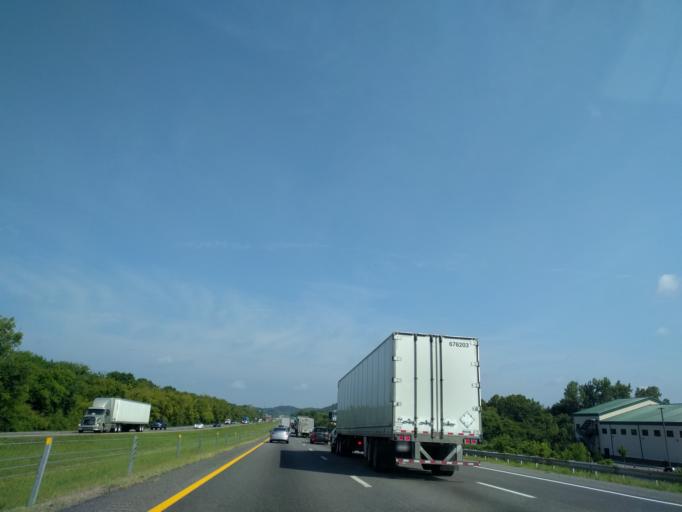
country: US
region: Tennessee
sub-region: Davidson County
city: Goodlettsville
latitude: 36.3270
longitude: -86.7064
